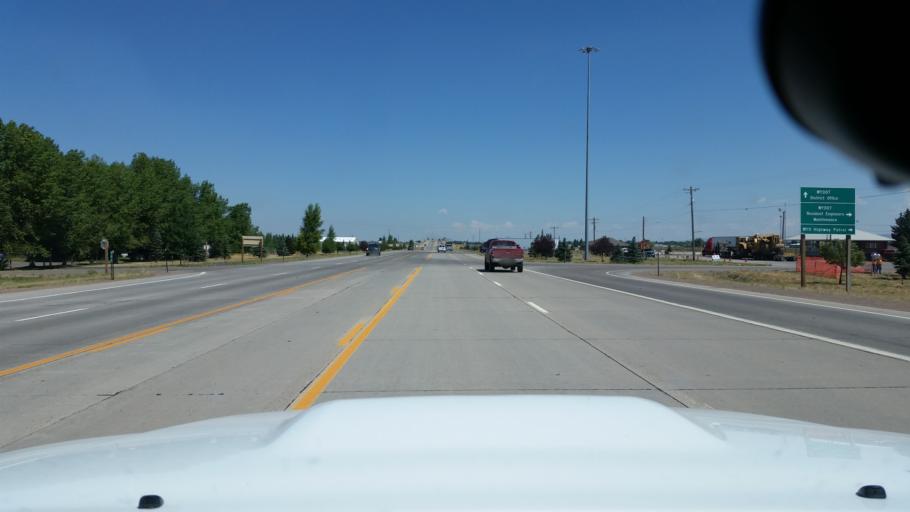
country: US
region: Wyoming
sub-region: Albany County
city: Laramie
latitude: 41.2820
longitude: -105.5916
